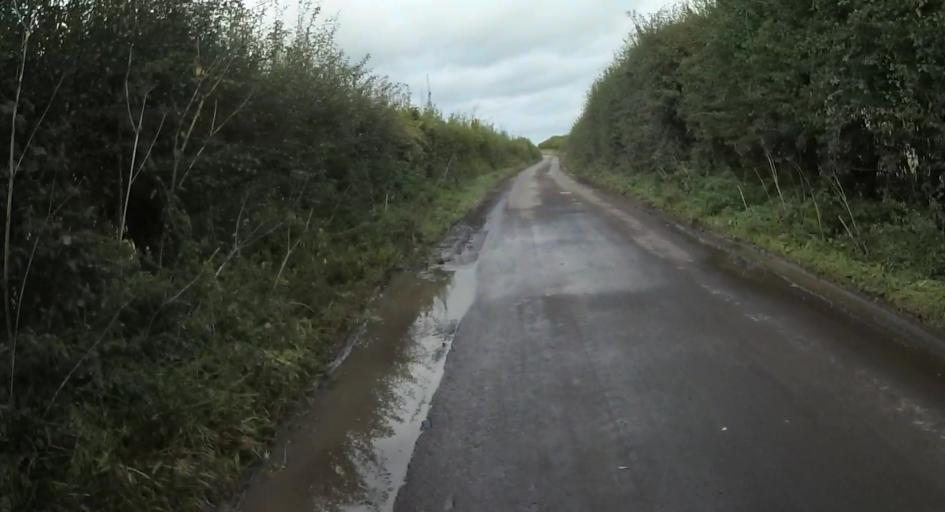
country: GB
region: England
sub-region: Hampshire
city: Alton
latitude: 51.1568
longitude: -0.9251
